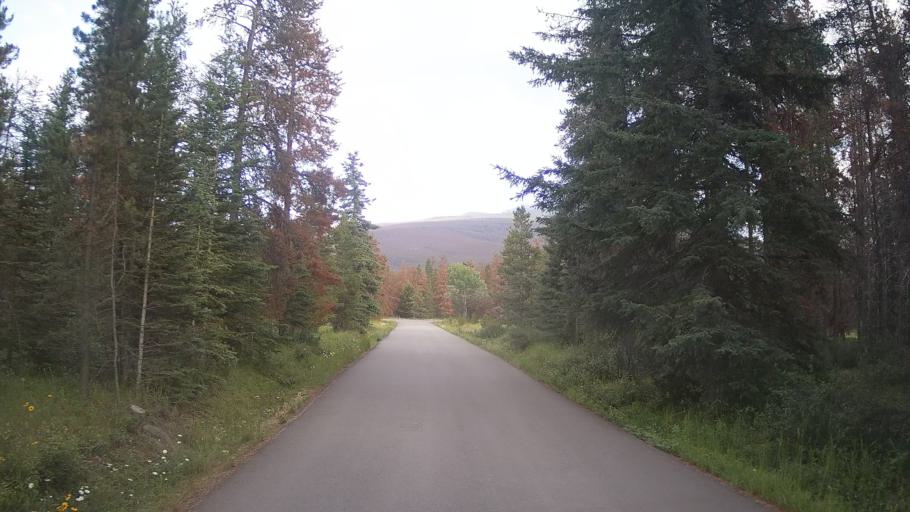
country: CA
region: Alberta
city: Jasper Park Lodge
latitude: 52.9301
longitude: -118.0312
